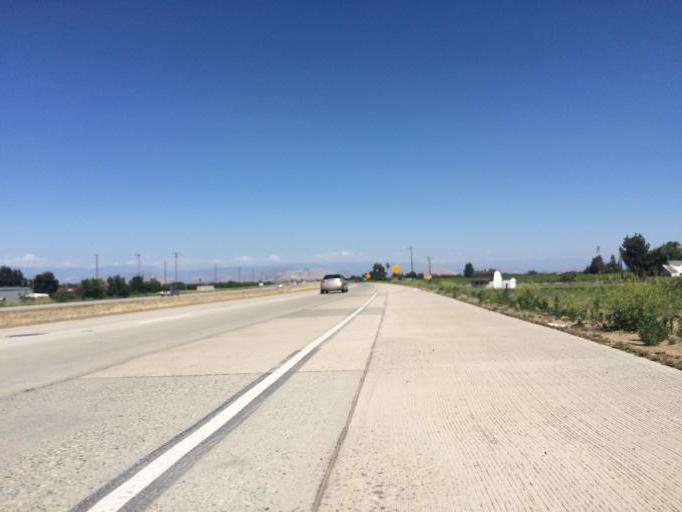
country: US
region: California
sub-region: Fresno County
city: Sunnyside
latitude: 36.7371
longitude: -119.6574
